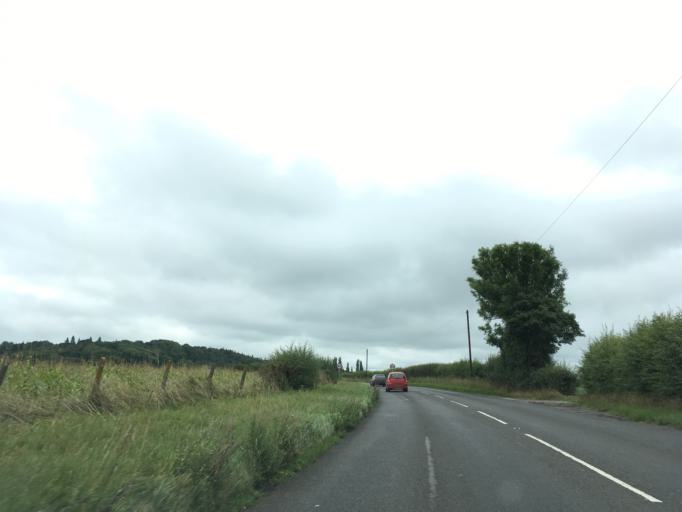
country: GB
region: England
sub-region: Bath and North East Somerset
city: Saltford
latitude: 51.3787
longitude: -2.4813
